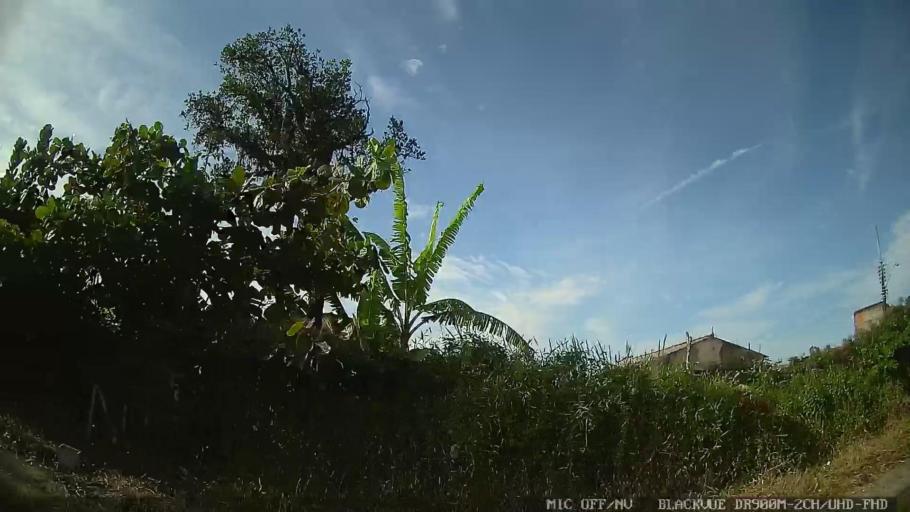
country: BR
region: Sao Paulo
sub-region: Itanhaem
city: Itanhaem
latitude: -24.1624
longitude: -46.7678
